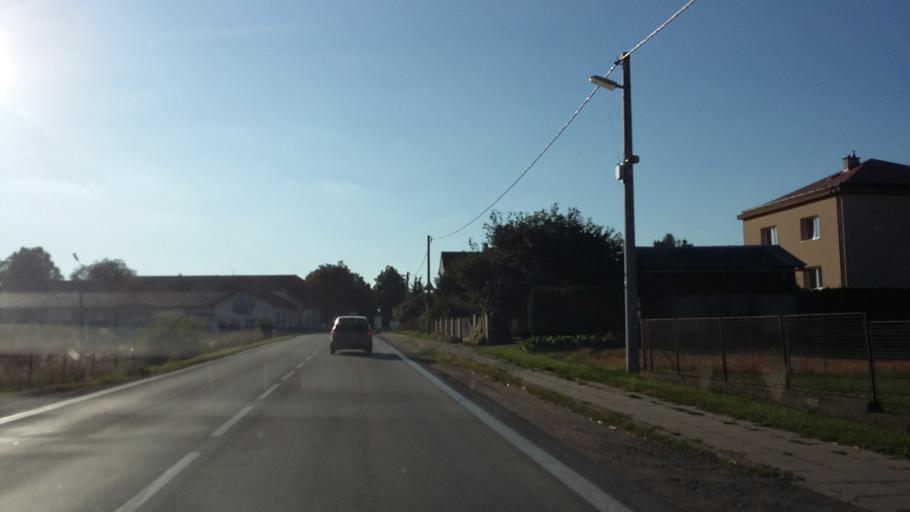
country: CZ
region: Vysocina
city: Merin
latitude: 49.3796
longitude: 15.9296
